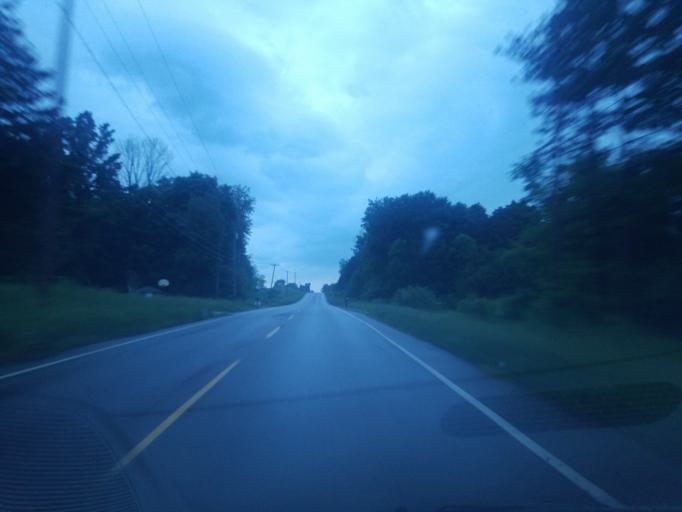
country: US
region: Ohio
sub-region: Mahoning County
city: Canfield
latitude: 40.9882
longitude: -80.7317
